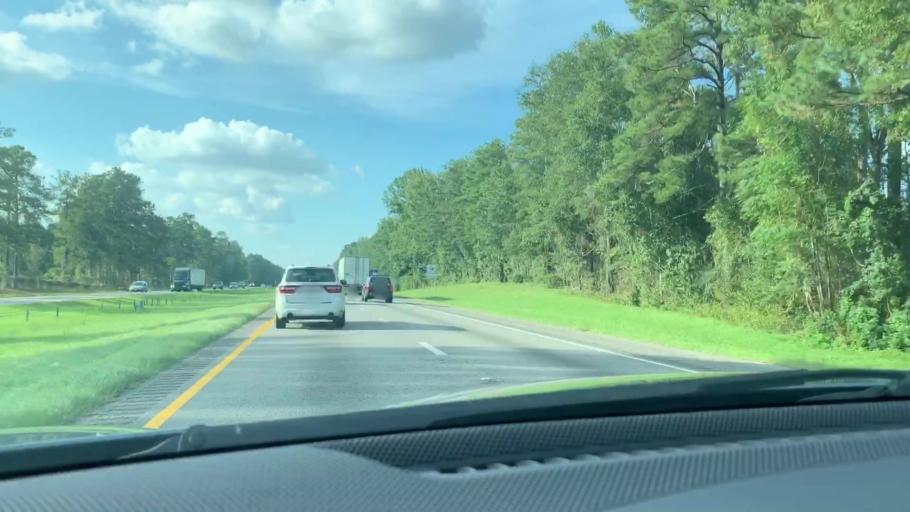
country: US
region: South Carolina
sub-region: Orangeburg County
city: Brookdale
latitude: 33.5421
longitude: -80.8101
